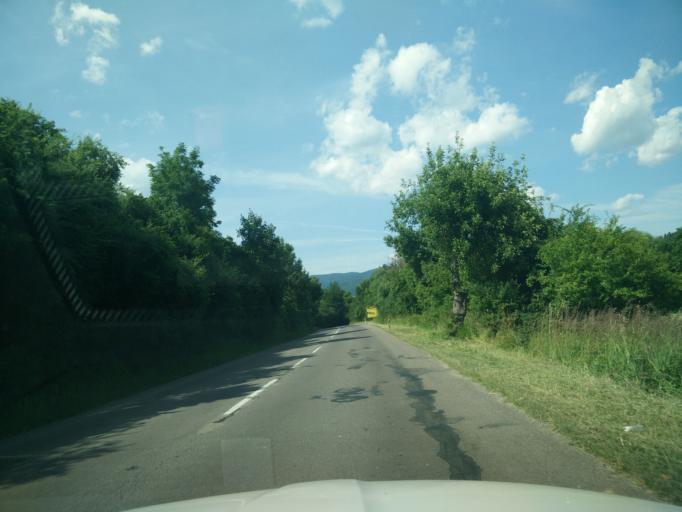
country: SK
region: Nitriansky
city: Prievidza
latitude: 48.8840
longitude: 18.6382
